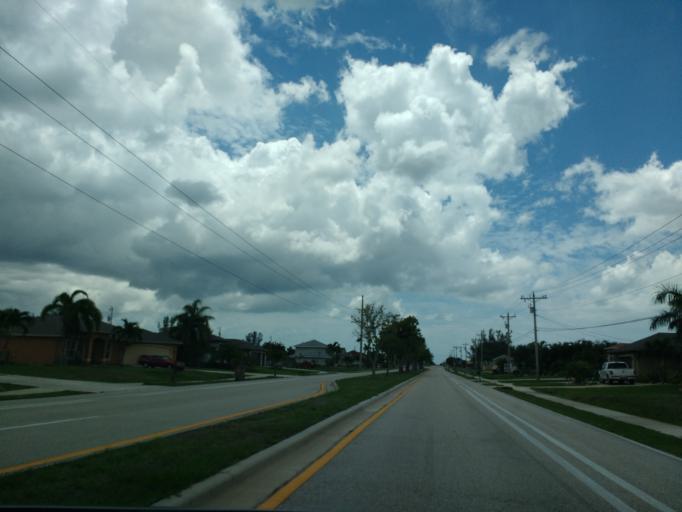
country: US
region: Florida
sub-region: Lee County
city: Cape Coral
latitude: 26.5711
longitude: -82.0174
